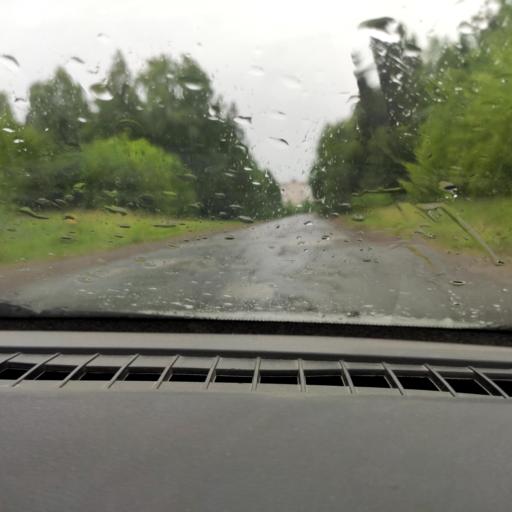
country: RU
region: Perm
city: Perm
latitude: 58.1056
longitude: 56.2826
